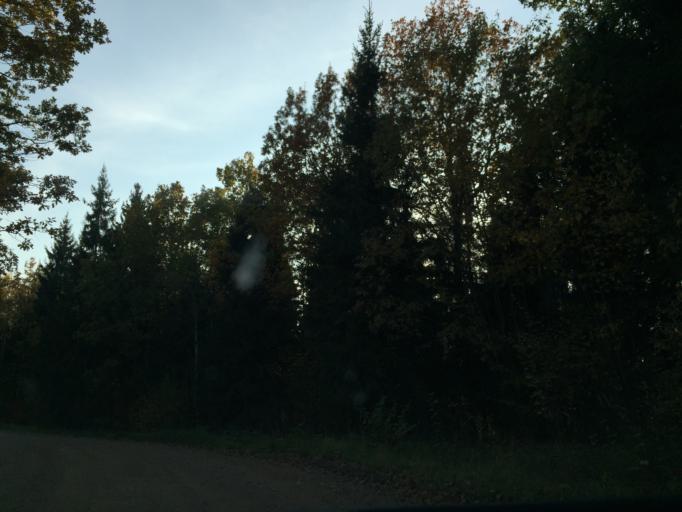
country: LV
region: Vainode
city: Vainode
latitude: 56.6035
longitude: 21.8248
